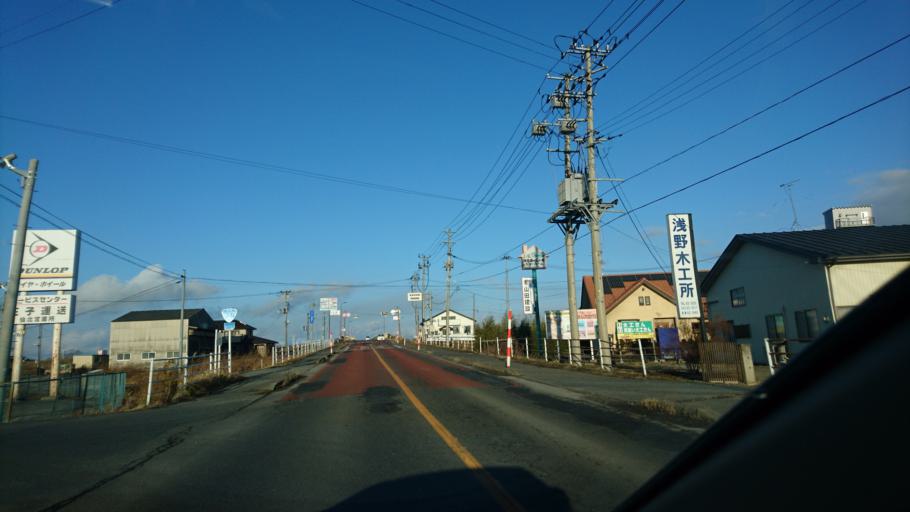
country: JP
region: Miyagi
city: Furukawa
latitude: 38.5555
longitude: 140.8554
